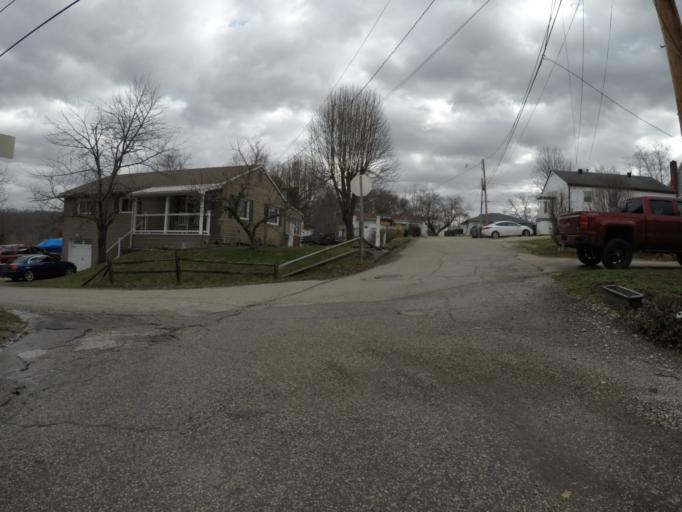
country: US
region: West Virginia
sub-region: Cabell County
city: Pea Ridge
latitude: 38.4081
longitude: -82.3802
